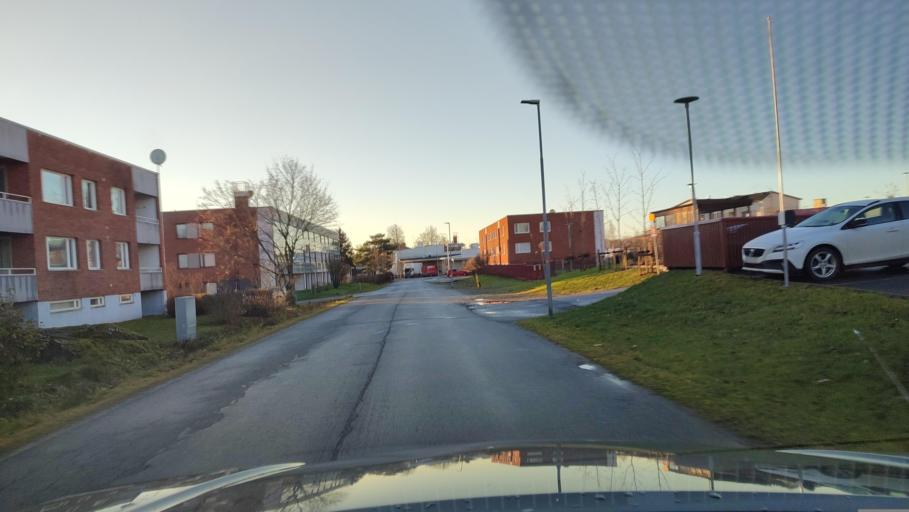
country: FI
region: Ostrobothnia
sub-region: Sydosterbotten
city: Naerpes
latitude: 62.4781
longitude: 21.3402
